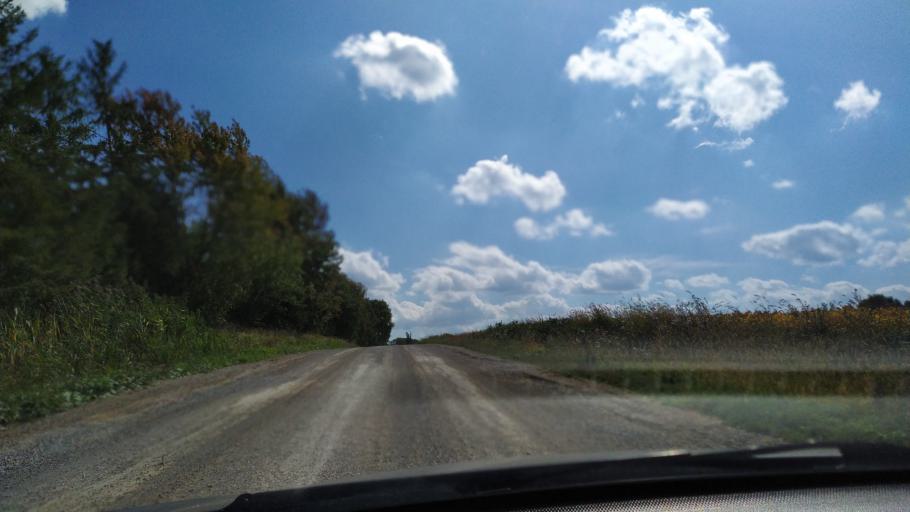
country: CA
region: Ontario
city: Stratford
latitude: 43.2892
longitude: -80.9310
